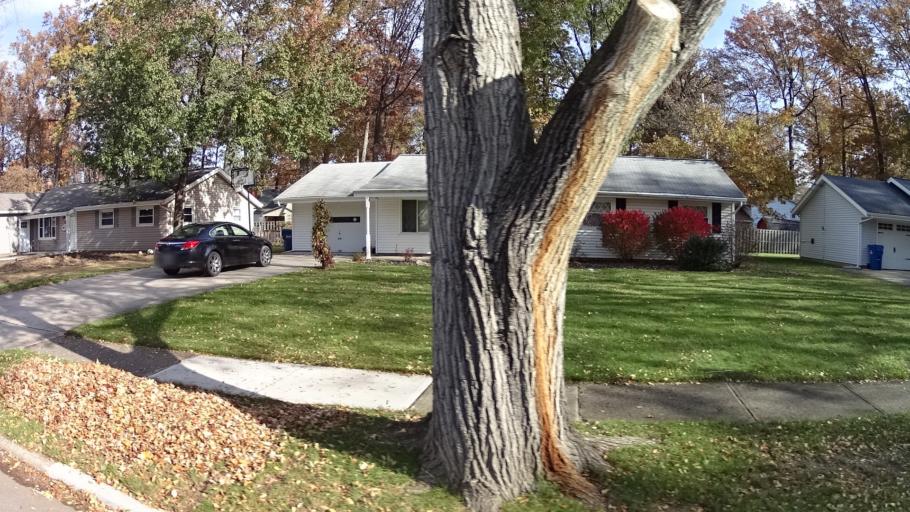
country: US
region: Ohio
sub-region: Lorain County
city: Avon Lake
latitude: 41.5035
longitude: -82.0289
